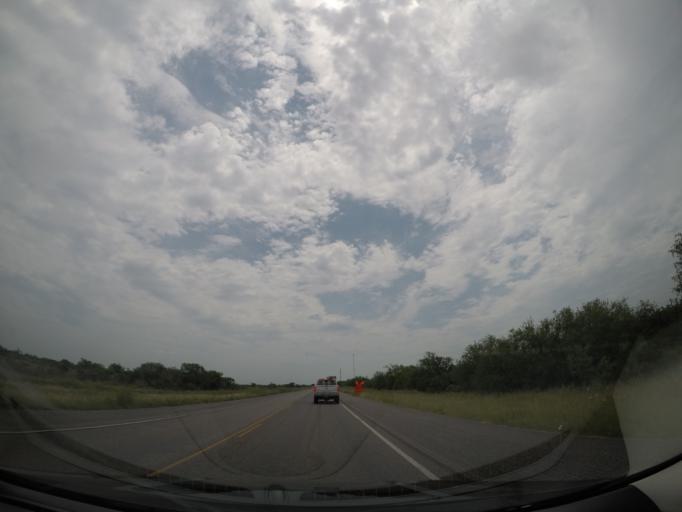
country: US
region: Texas
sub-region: Val Verde County
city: Laughlin Air Force Base
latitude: 29.3862
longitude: -100.7466
